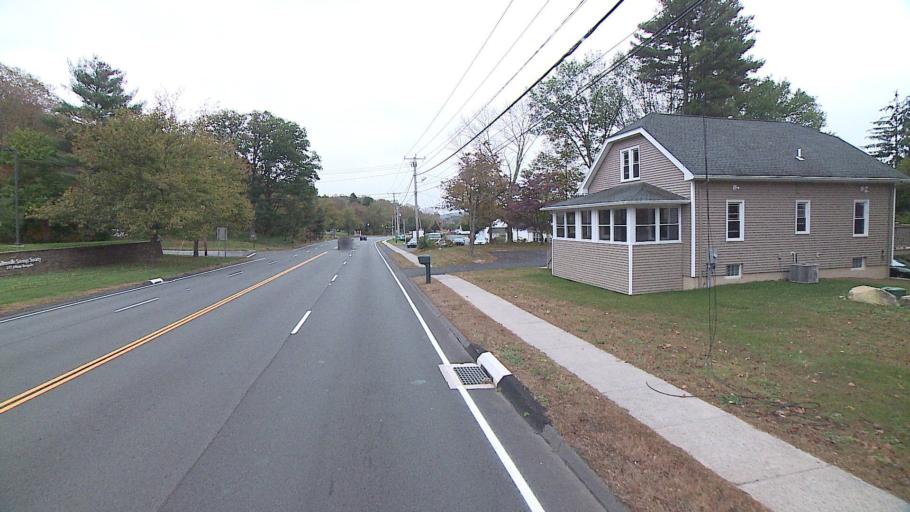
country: US
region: Connecticut
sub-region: Hartford County
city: Canton Valley
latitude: 41.8301
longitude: -72.9037
